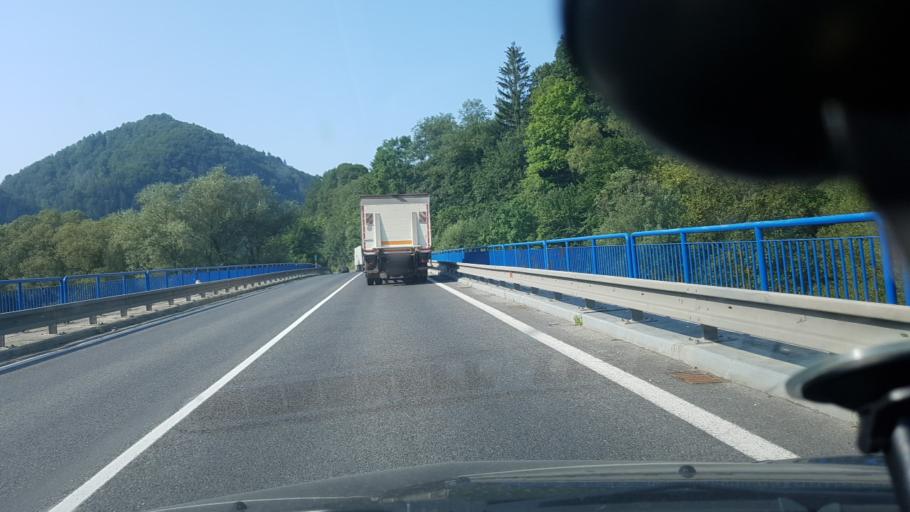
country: SK
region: Zilinsky
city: Tvrdosin
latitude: 49.2712
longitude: 19.4607
